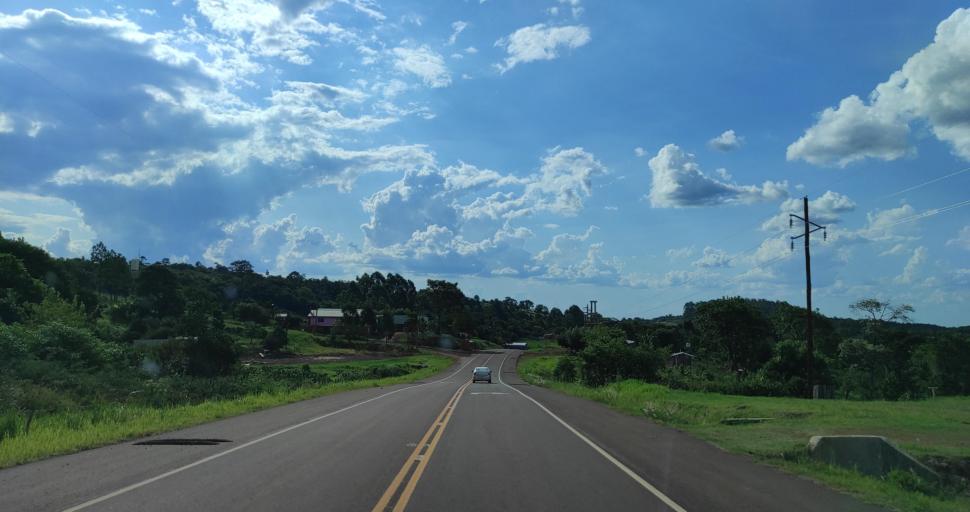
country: AR
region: Misiones
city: Bernardo de Irigoyen
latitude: -26.3873
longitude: -53.9103
